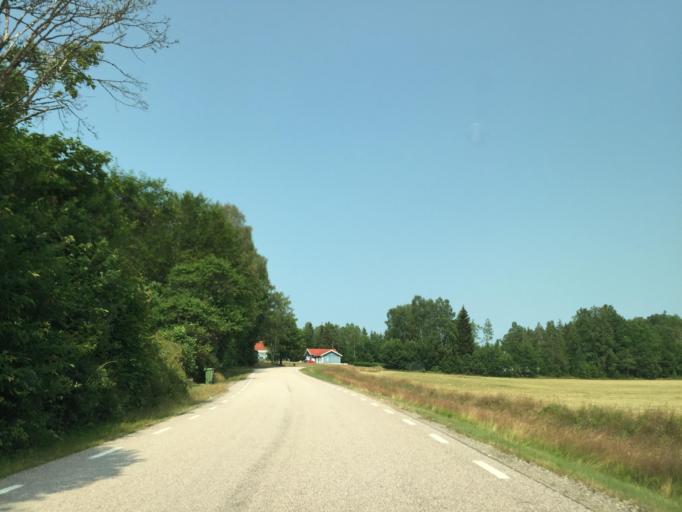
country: SE
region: Vaestra Goetaland
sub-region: Lilla Edets Kommun
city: Lilla Edet
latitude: 58.1714
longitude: 12.0818
